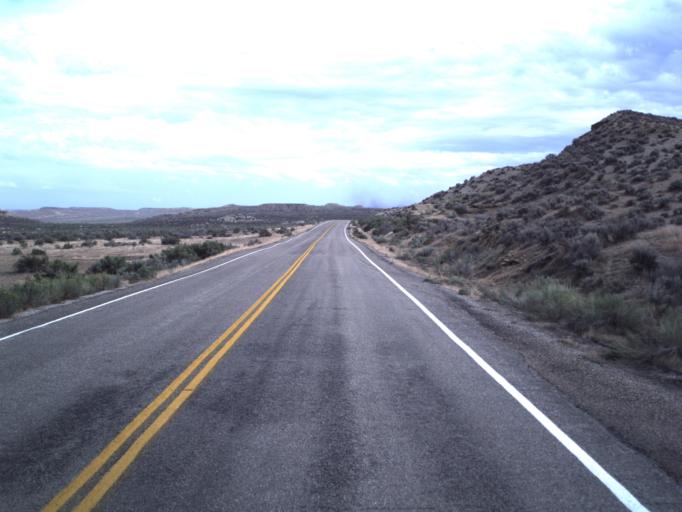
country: US
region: Colorado
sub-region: Rio Blanco County
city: Rangely
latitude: 40.0475
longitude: -109.1883
